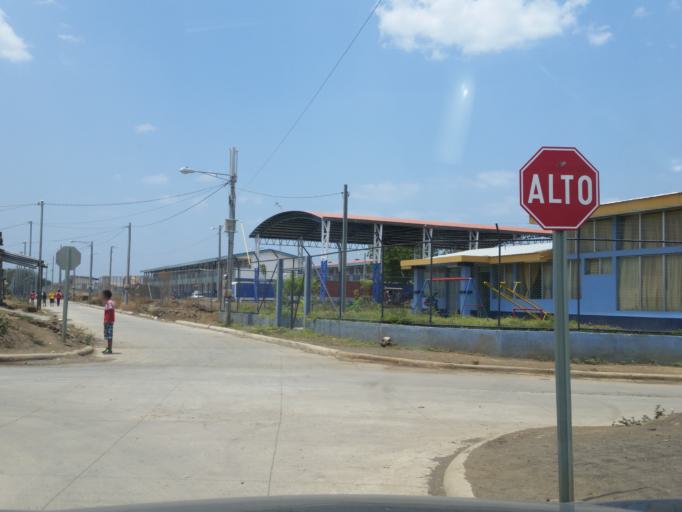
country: NI
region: Managua
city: Tipitapa
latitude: 12.1307
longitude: -86.1579
